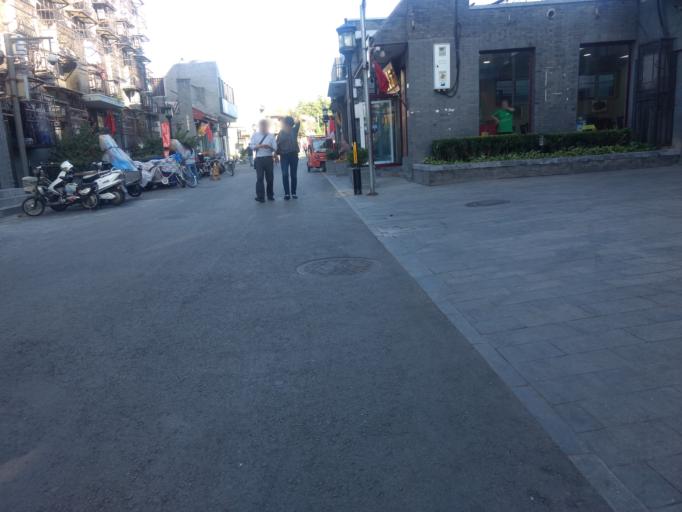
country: CN
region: Beijing
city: Beijing
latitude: 39.8977
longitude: 116.3874
